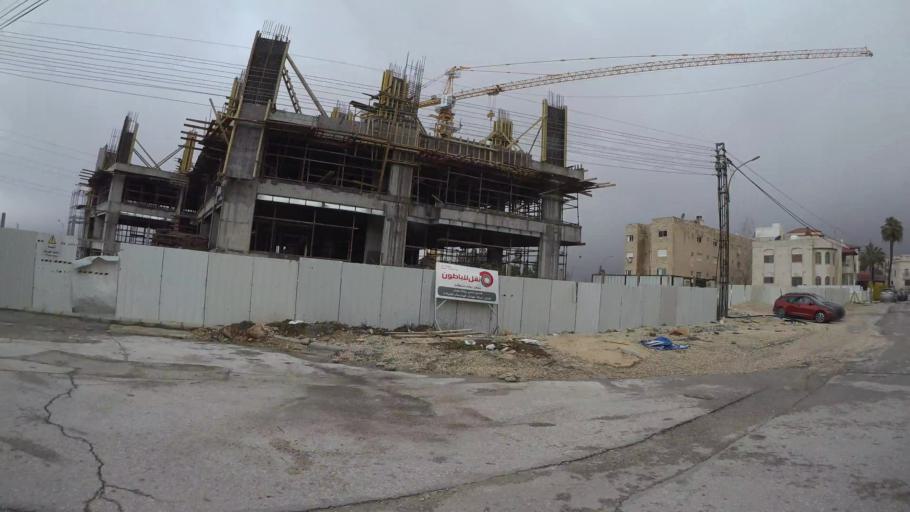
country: JO
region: Amman
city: Wadi as Sir
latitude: 31.9438
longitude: 35.8599
